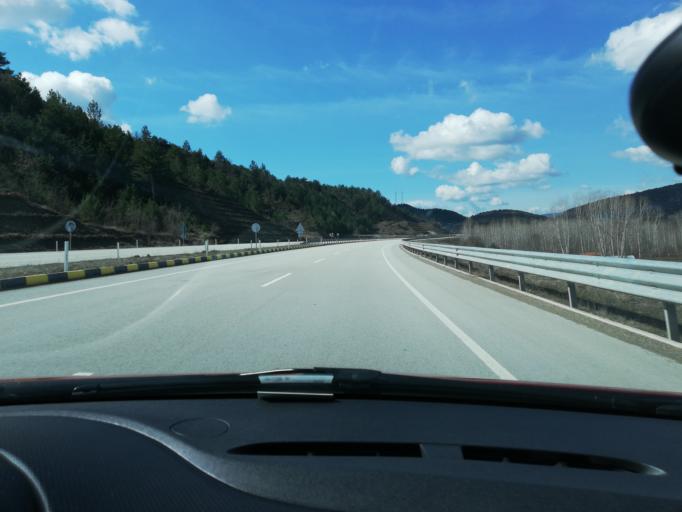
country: TR
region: Kastamonu
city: Igdir
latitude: 41.2322
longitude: 33.0437
